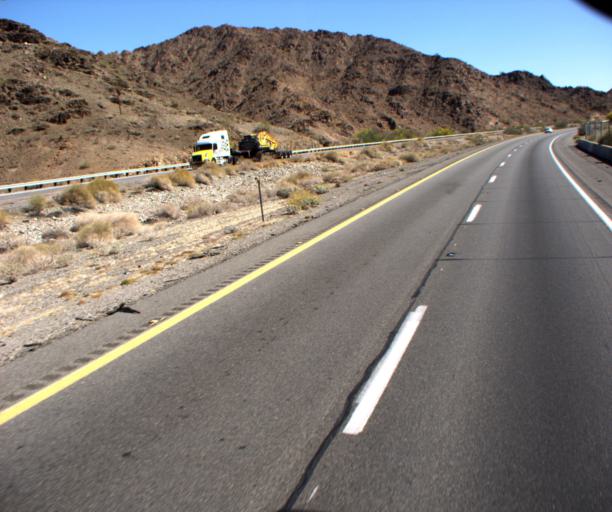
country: US
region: Arizona
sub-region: La Paz County
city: Quartzsite
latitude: 33.6465
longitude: -114.3761
